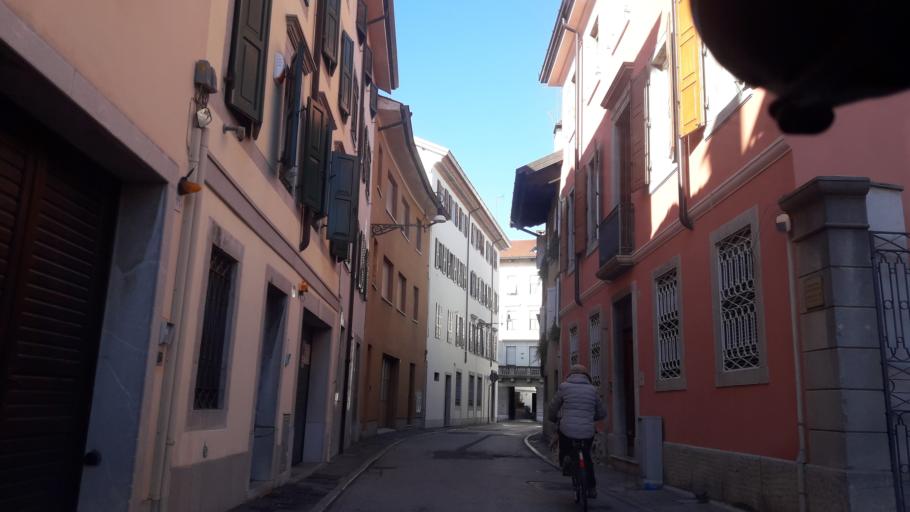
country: IT
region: Friuli Venezia Giulia
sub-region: Provincia di Udine
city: Udine
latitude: 46.0603
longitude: 13.2303
